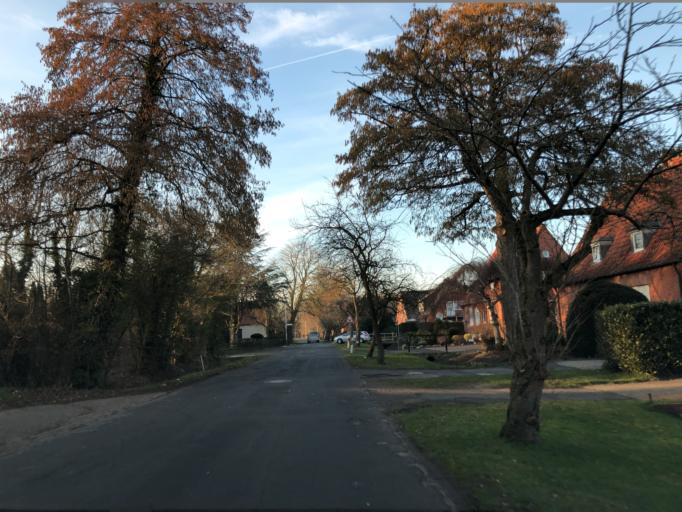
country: DE
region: Lower Saxony
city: Papenburg
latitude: 53.0785
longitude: 7.3821
